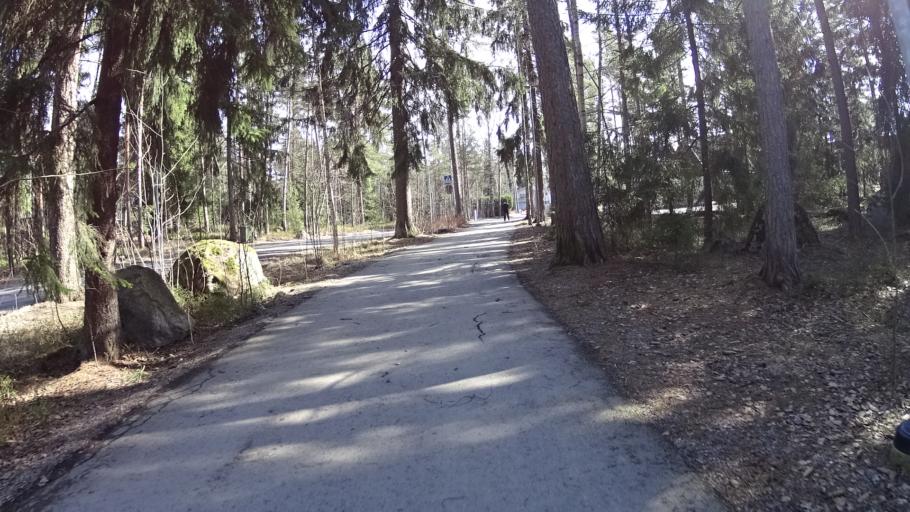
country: FI
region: Uusimaa
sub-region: Helsinki
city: Kauniainen
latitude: 60.2182
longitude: 24.7038
